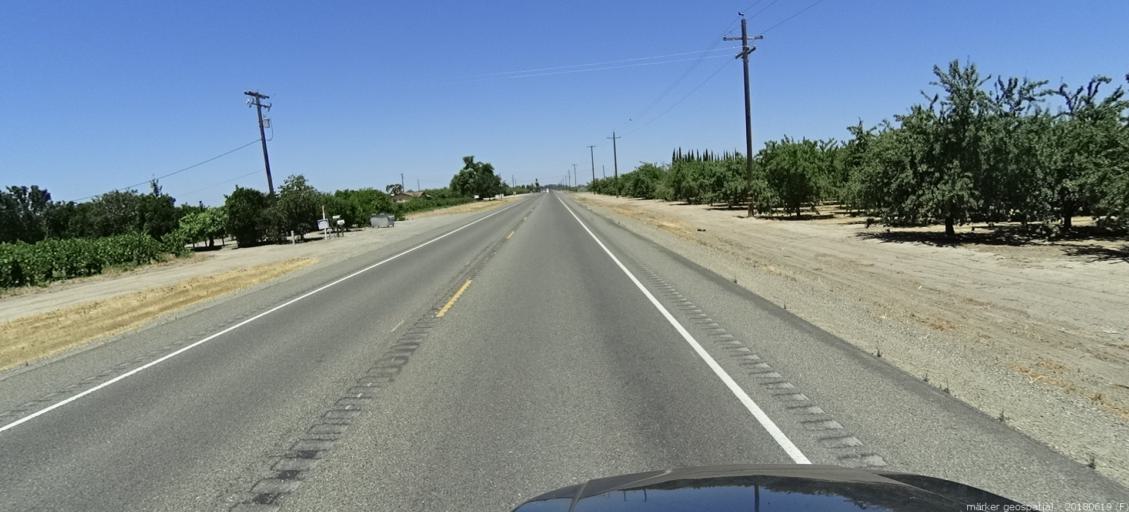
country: US
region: California
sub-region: Madera County
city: Parkwood
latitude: 36.8638
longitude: -120.0557
